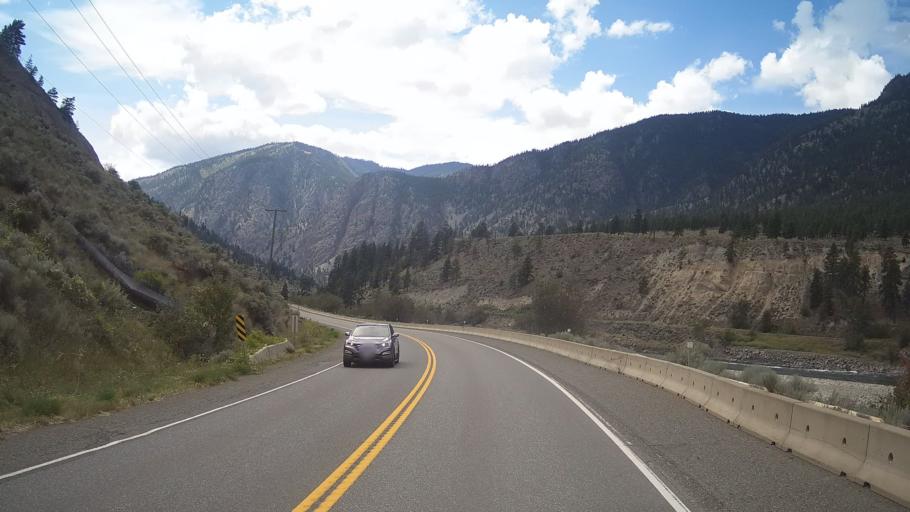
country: CA
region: British Columbia
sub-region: Thompson-Nicola Regional District
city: Ashcroft
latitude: 50.4017
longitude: -121.3782
